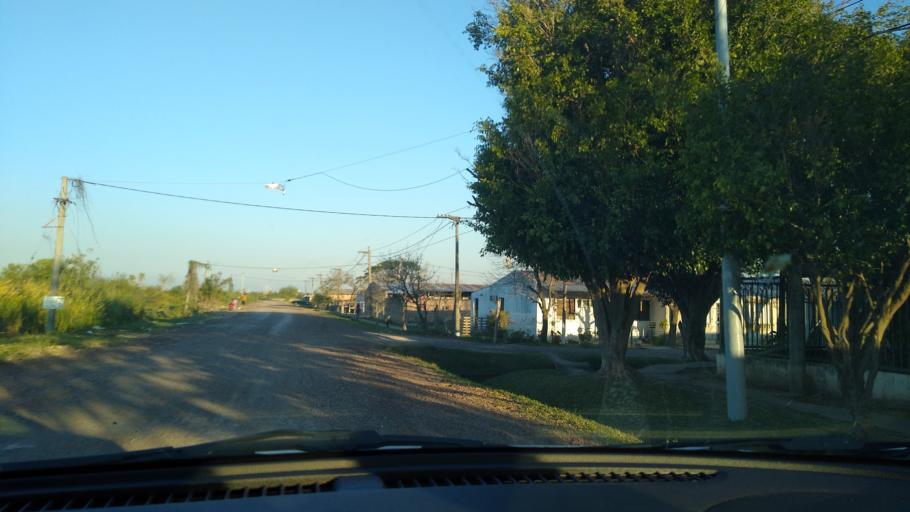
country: AR
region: Chaco
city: Puerto Vilelas
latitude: -27.5039
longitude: -58.9557
